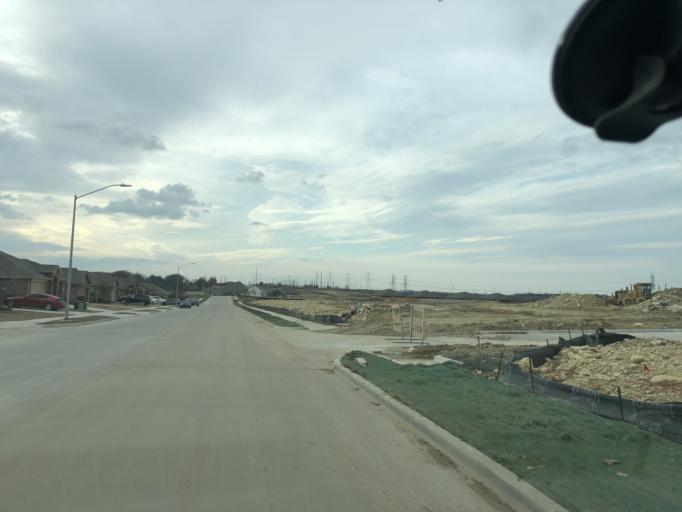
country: US
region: Texas
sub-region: Tarrant County
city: Saginaw
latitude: 32.9031
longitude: -97.3669
